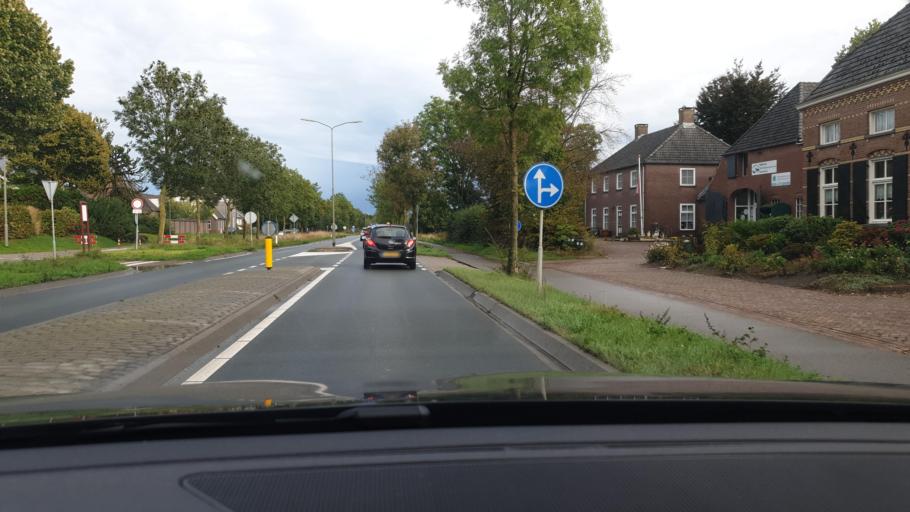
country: NL
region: North Brabant
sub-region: Gemeente Landerd
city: Schaijk
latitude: 51.8004
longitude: 5.6271
